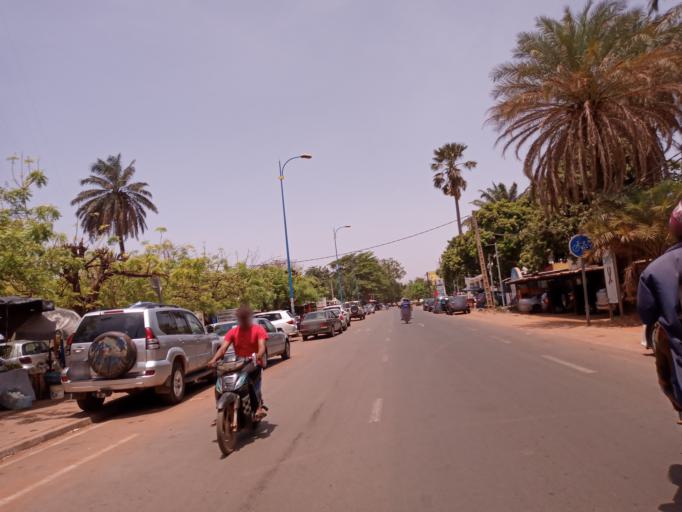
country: ML
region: Bamako
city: Bamako
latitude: 12.6331
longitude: -7.9995
